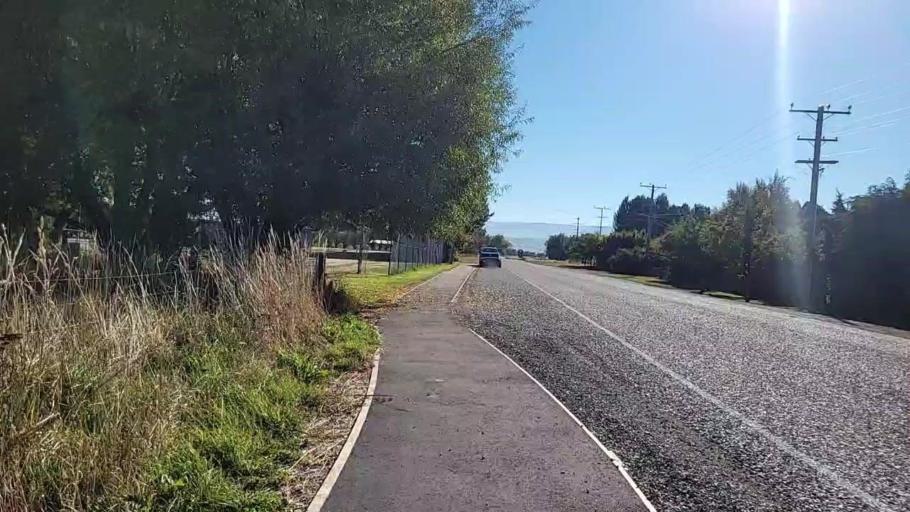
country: NZ
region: Otago
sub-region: Queenstown-Lakes District
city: Wanaka
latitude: -45.0034
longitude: 169.9165
